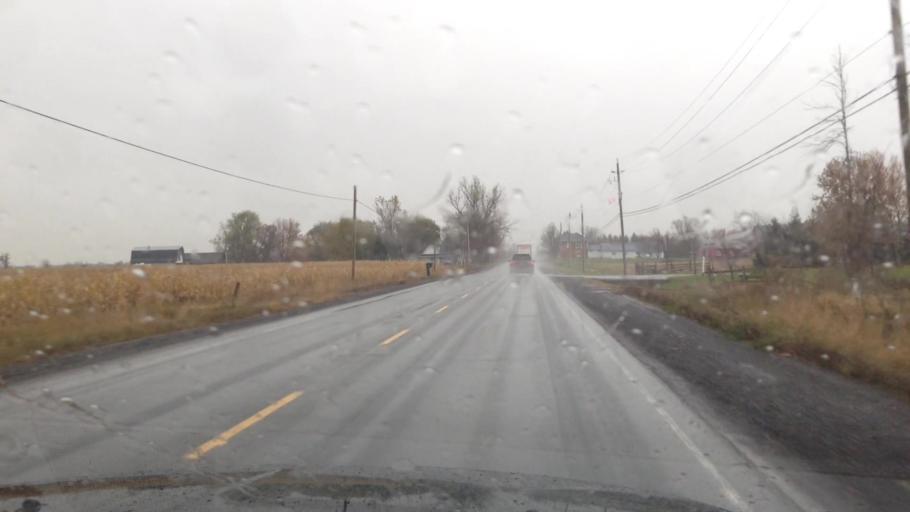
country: CA
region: Ontario
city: Bourget
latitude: 45.2950
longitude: -75.3253
